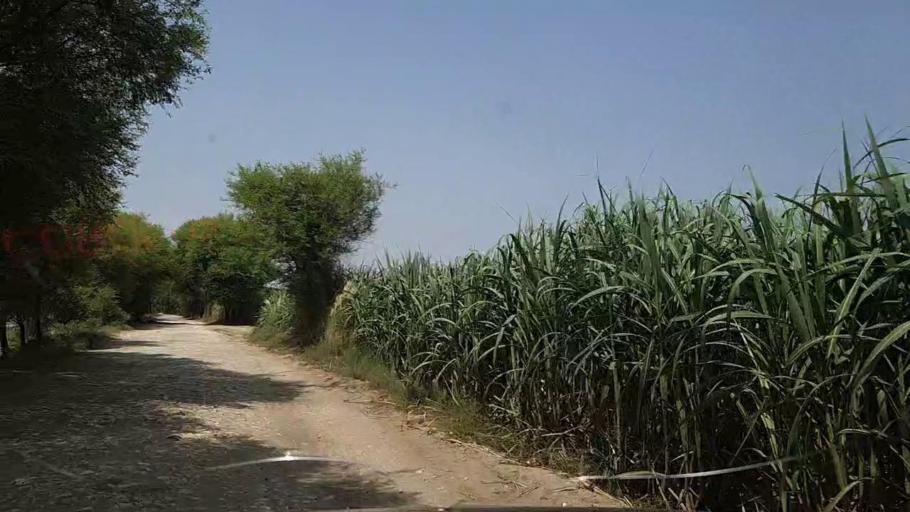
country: PK
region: Sindh
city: Ghotki
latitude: 28.0829
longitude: 69.3117
